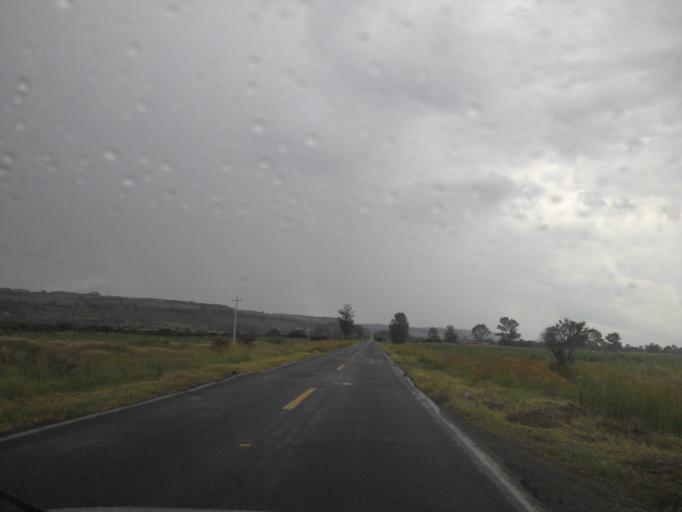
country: MX
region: Jalisco
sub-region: Arandas
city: Santiaguito (Santiaguito de Velazquez)
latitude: 20.8035
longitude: -102.2313
